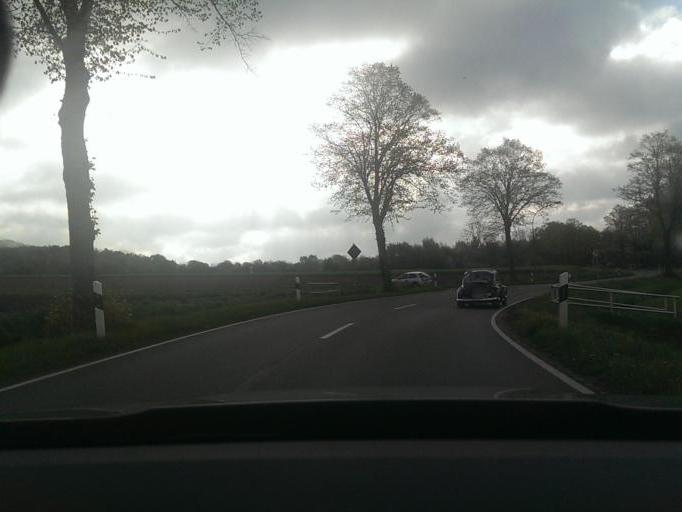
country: DE
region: Lower Saxony
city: Hameln
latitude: 52.1581
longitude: 9.3641
